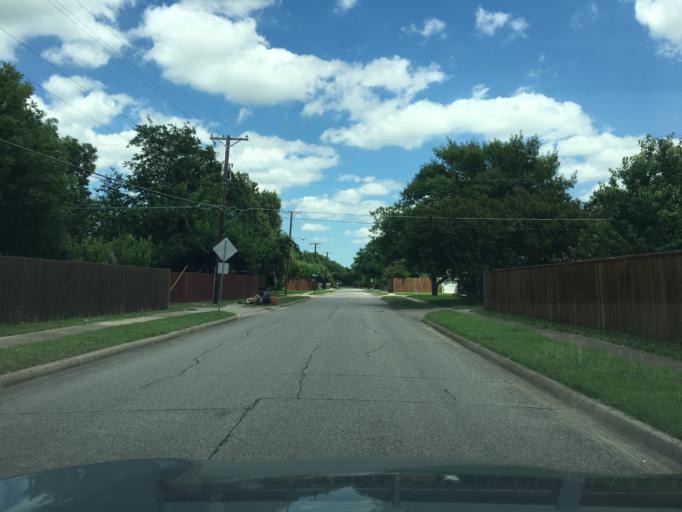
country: US
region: Texas
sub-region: Dallas County
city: Richardson
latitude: 32.9502
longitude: -96.7130
